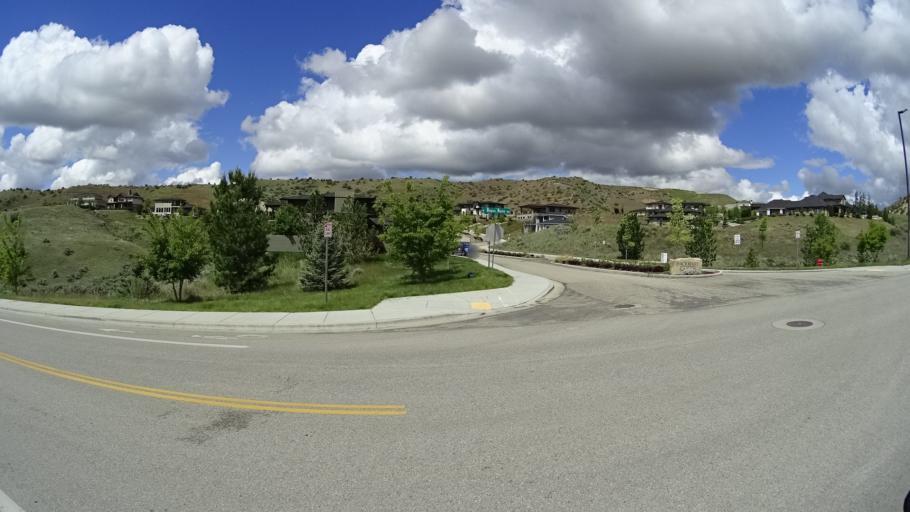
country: US
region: Idaho
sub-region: Ada County
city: Boise
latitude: 43.6602
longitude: -116.1898
